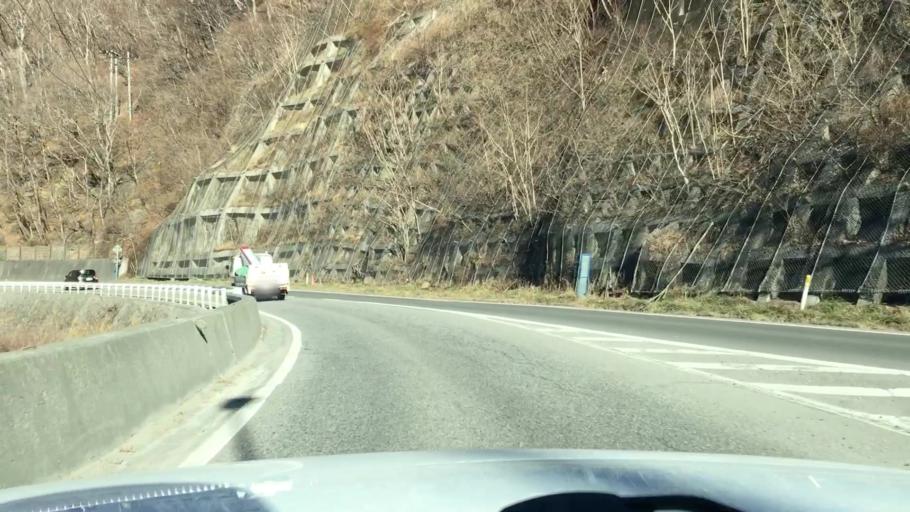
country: JP
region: Iwate
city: Miyako
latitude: 39.6252
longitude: 141.8237
